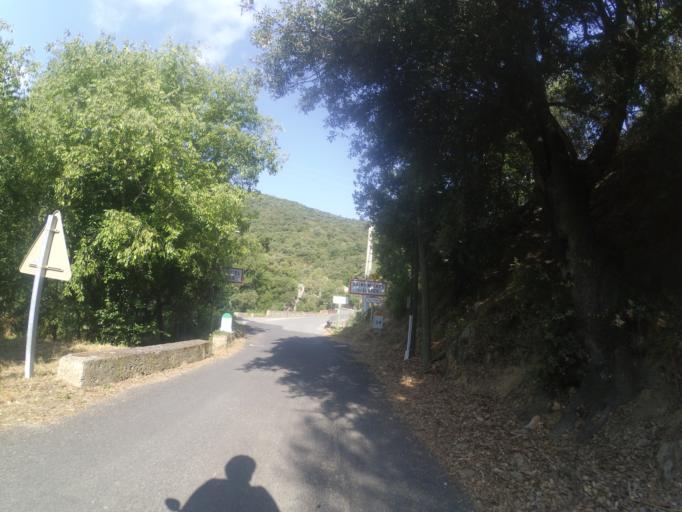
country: FR
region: Languedoc-Roussillon
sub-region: Departement des Pyrenees-Orientales
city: Ille-sur-Tet
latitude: 42.6450
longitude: 2.6250
